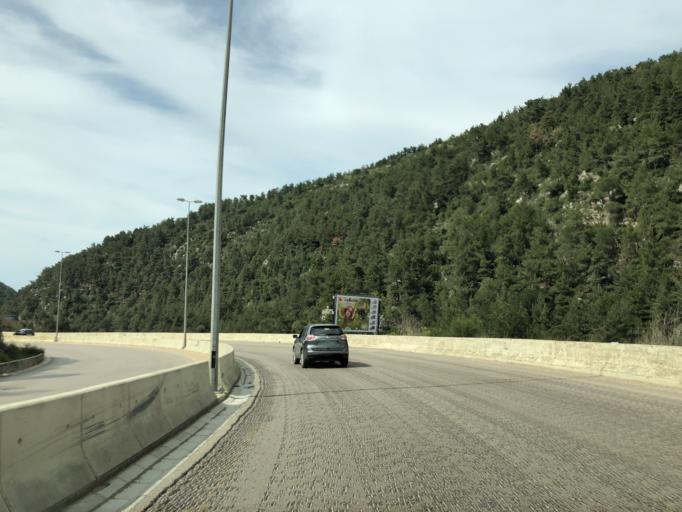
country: LB
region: Mont-Liban
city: Bhamdoun el Mhatta
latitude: 33.8943
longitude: 35.6573
